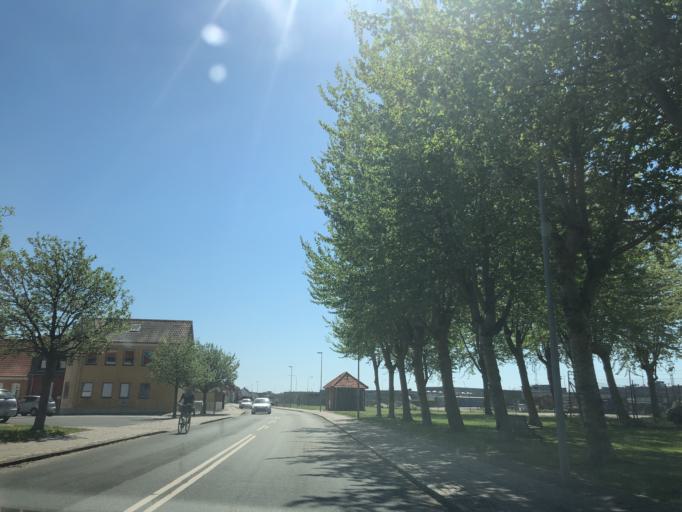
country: DK
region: Zealand
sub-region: Slagelse Kommune
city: Korsor
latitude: 55.3327
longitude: 11.1354
